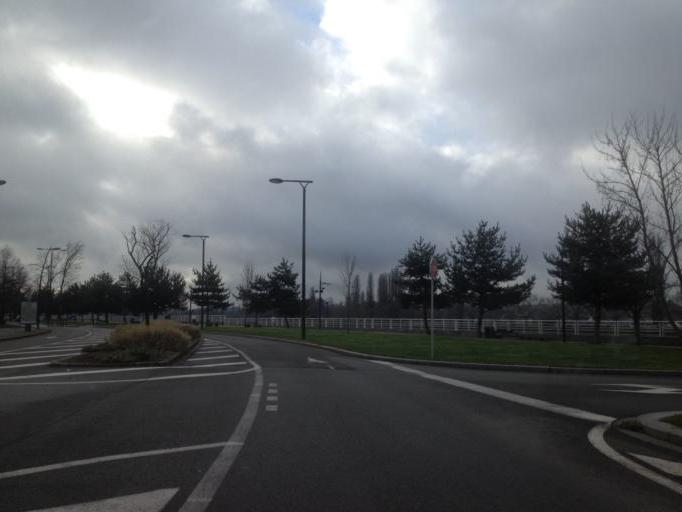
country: FR
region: Auvergne
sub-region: Departement de l'Allier
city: Vichy
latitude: 46.1350
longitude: 3.4144
